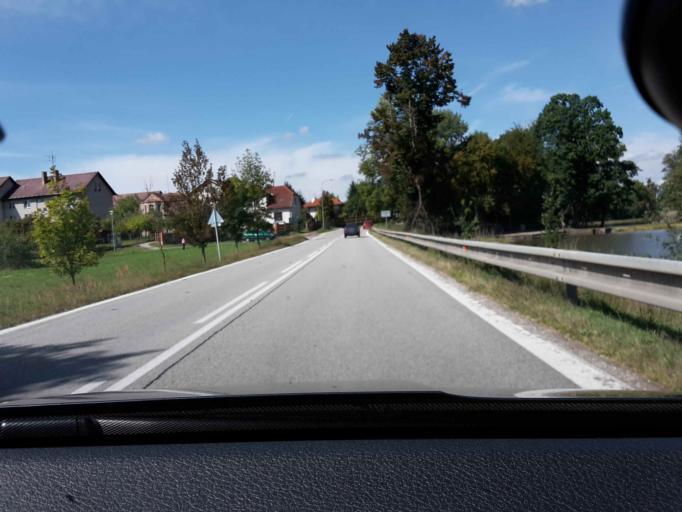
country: CZ
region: Jihocesky
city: Kardasova Recice
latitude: 49.1796
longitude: 14.8614
